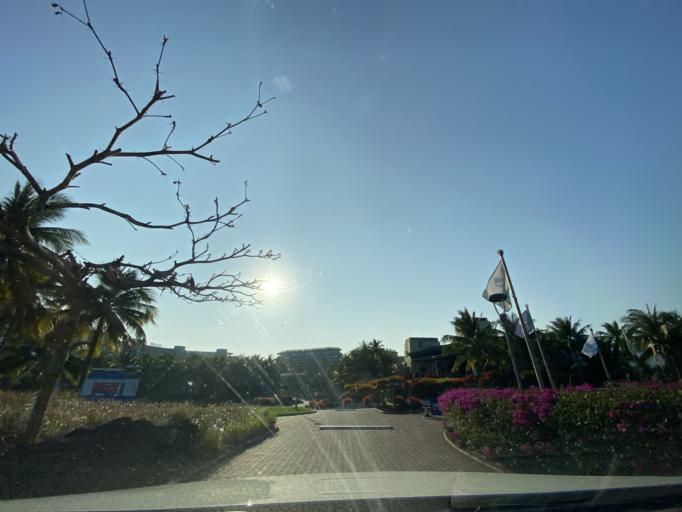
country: CN
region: Hainan
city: Xincun
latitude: 18.4186
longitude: 109.9527
